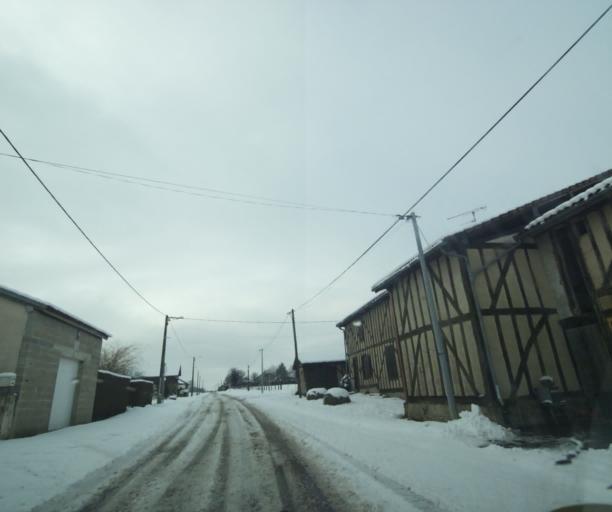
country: FR
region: Champagne-Ardenne
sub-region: Departement de la Haute-Marne
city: Montier-en-Der
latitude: 48.5218
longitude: 4.7036
